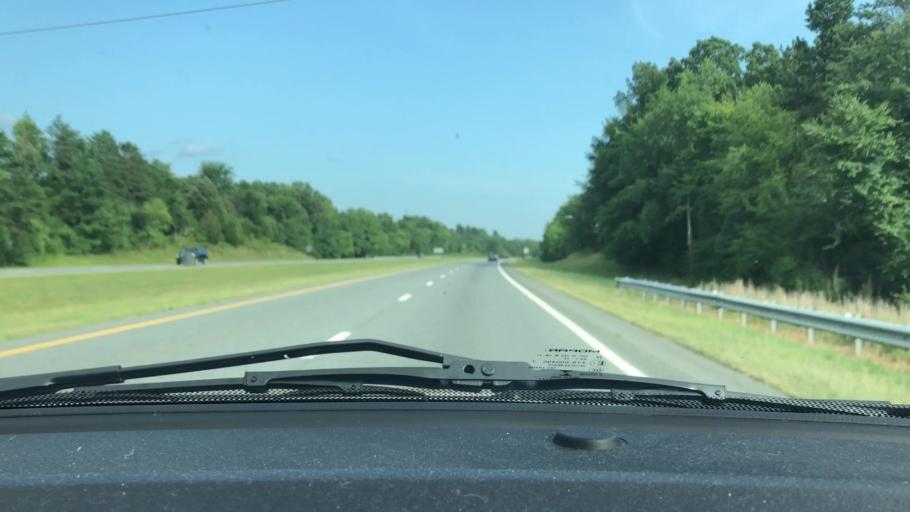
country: US
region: North Carolina
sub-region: Guilford County
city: Forest Oaks
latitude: 35.9574
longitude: -79.6959
